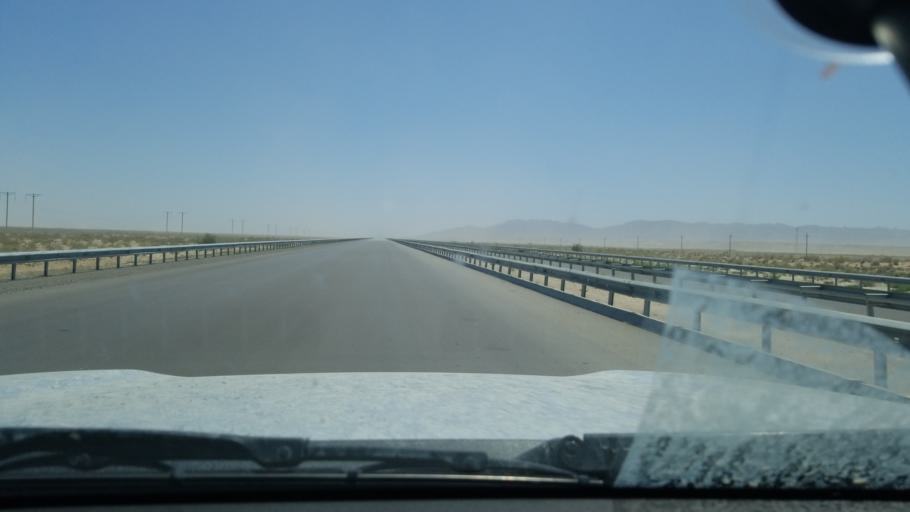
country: TM
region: Balkan
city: Gazanjyk
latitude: 39.2604
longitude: 55.3185
